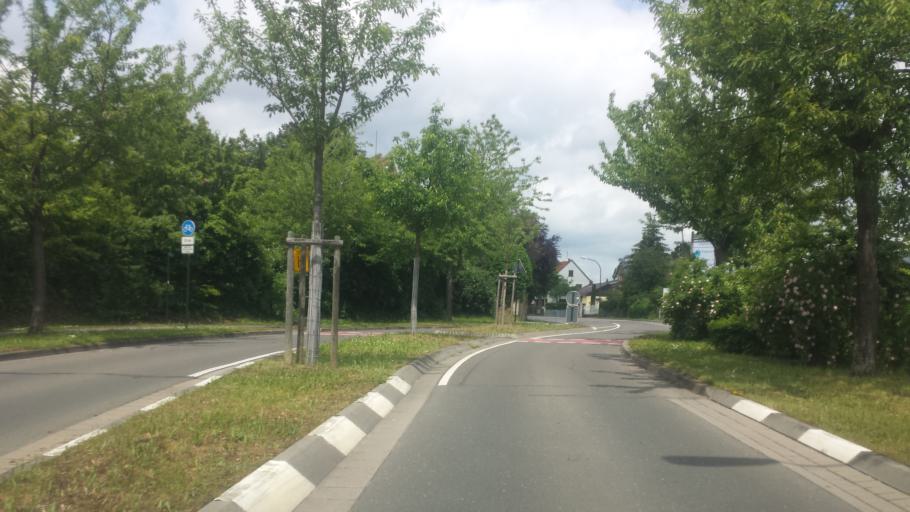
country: DE
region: Rheinland-Pfalz
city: Bad Duerkheim
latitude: 49.4532
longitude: 8.1765
